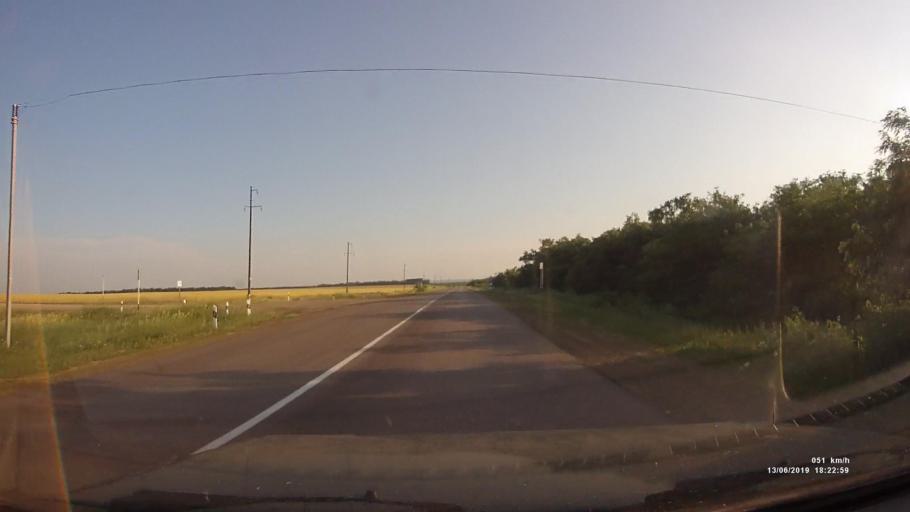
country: RU
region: Rostov
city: Kazanskaya
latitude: 49.8534
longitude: 41.2748
